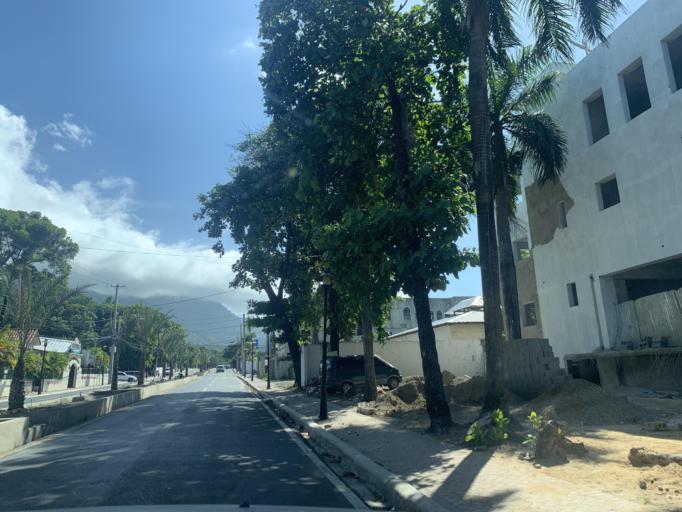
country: DO
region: Puerto Plata
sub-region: Puerto Plata
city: Puerto Plata
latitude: 19.7848
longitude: -70.6702
